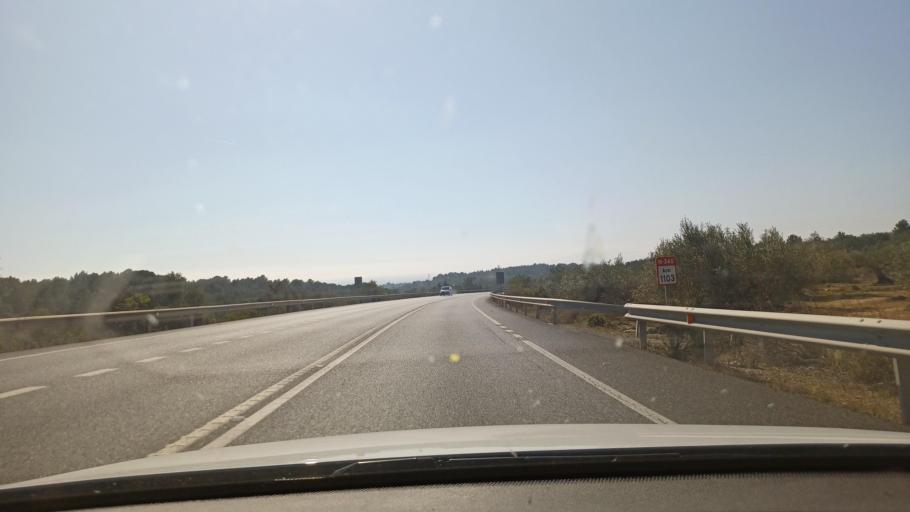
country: ES
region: Catalonia
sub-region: Provincia de Tarragona
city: El Perello
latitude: 40.8557
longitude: 0.7143
